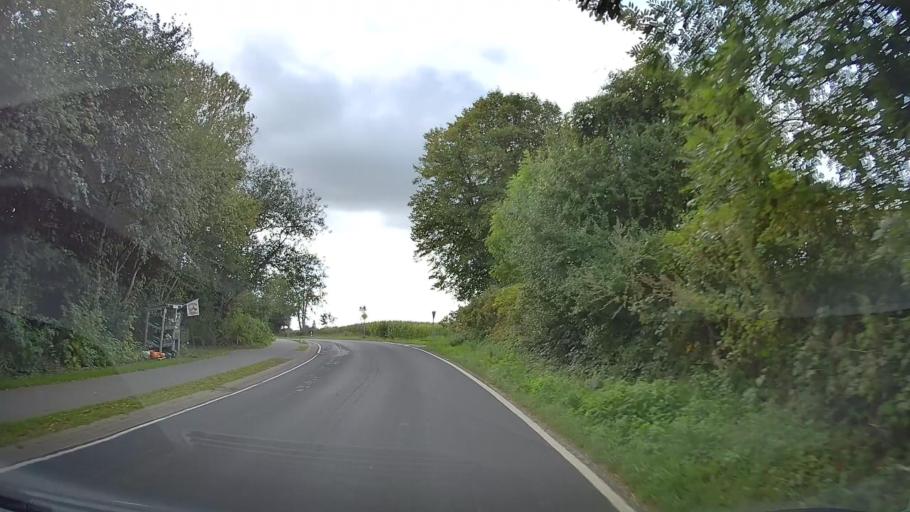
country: DE
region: Schleswig-Holstein
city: Steinberg
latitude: 54.7625
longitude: 9.8015
